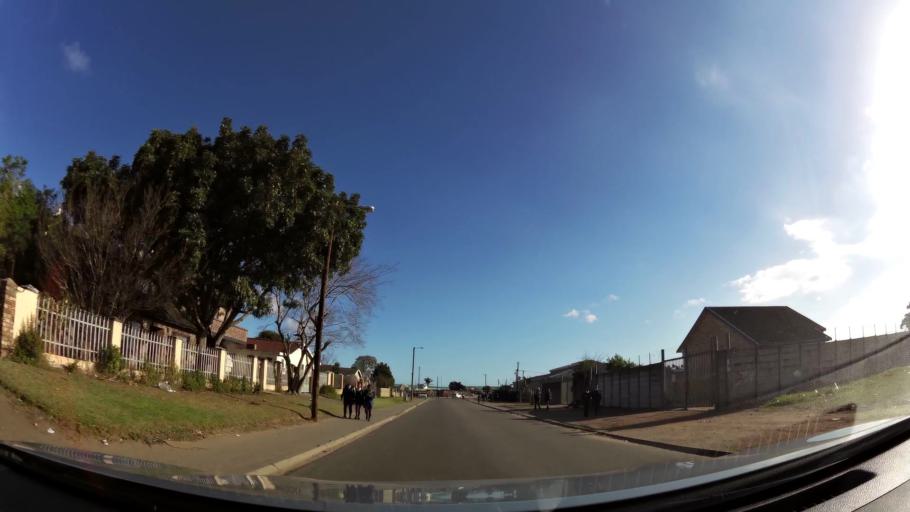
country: ZA
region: Western Cape
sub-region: Eden District Municipality
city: George
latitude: -33.9915
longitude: 22.4767
